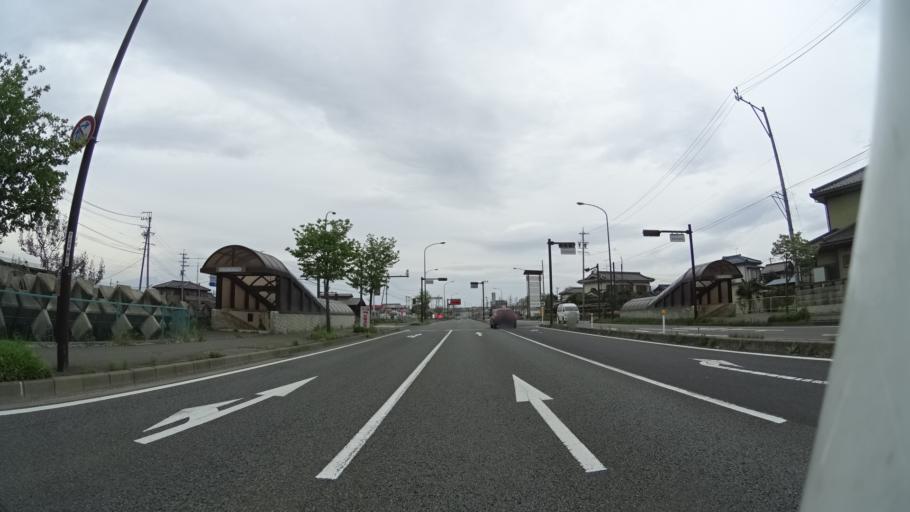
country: JP
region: Nagano
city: Nagano-shi
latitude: 36.5426
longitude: 138.1240
